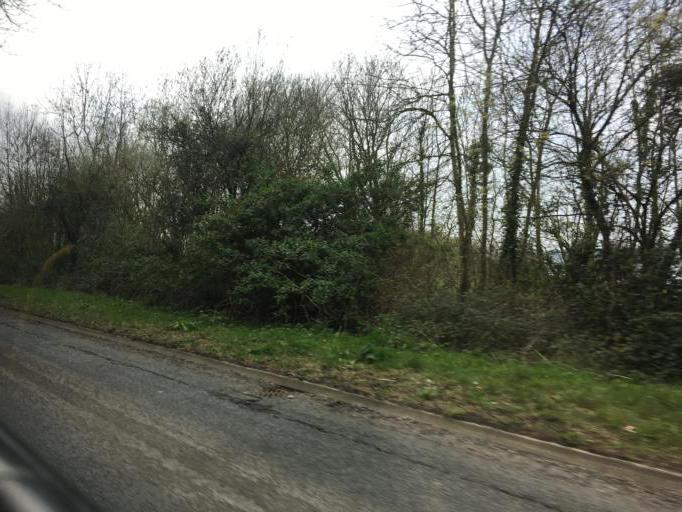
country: GB
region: Wales
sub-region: Gwynedd
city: Y Felinheli
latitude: 53.1725
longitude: -4.2277
